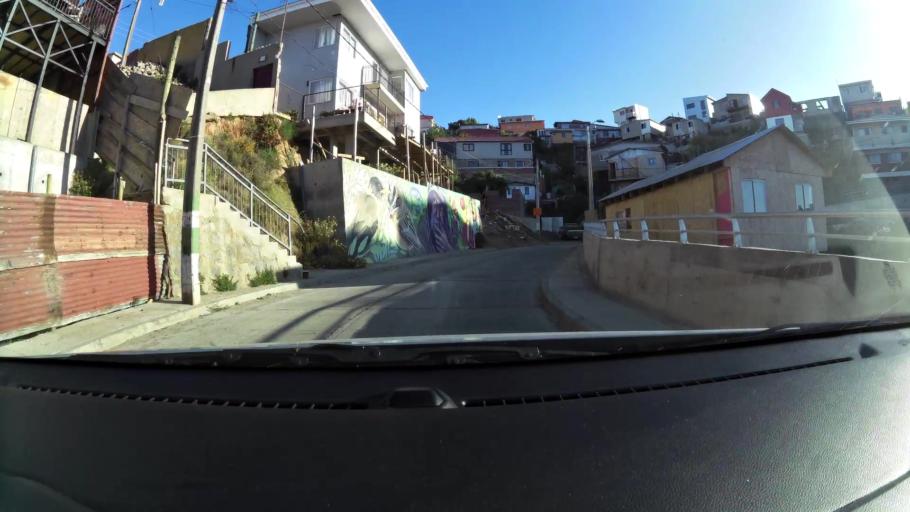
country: CL
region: Valparaiso
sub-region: Provincia de Valparaiso
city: Valparaiso
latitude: -33.0588
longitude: -71.6133
